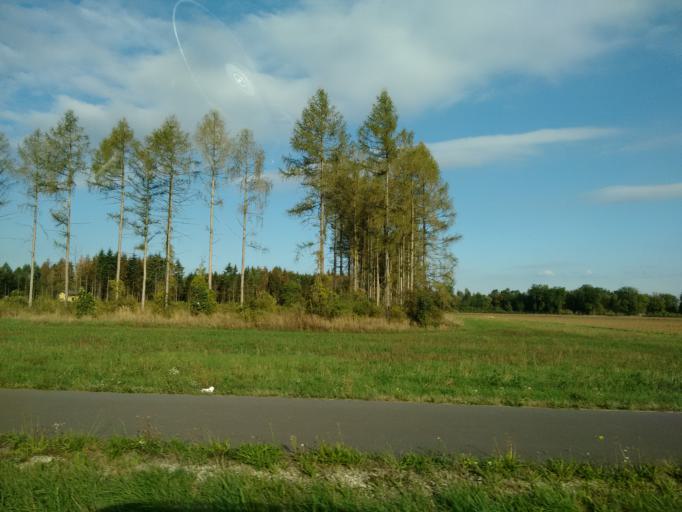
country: AT
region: Upper Austria
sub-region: Politischer Bezirk Linz-Land
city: Horsching
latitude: 48.2244
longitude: 14.2045
